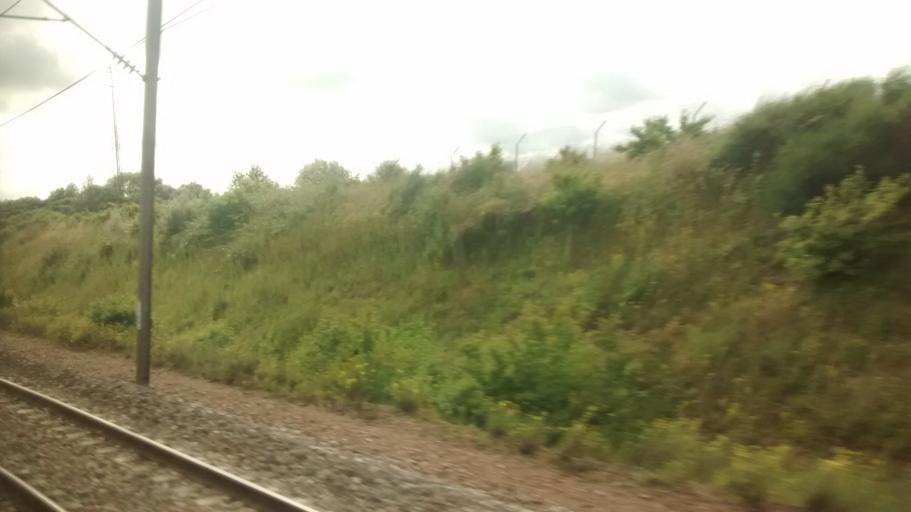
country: FR
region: Centre
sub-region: Departement d'Eure-et-Loir
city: Aunay-sous-Auneau
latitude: 48.4692
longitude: 1.8383
